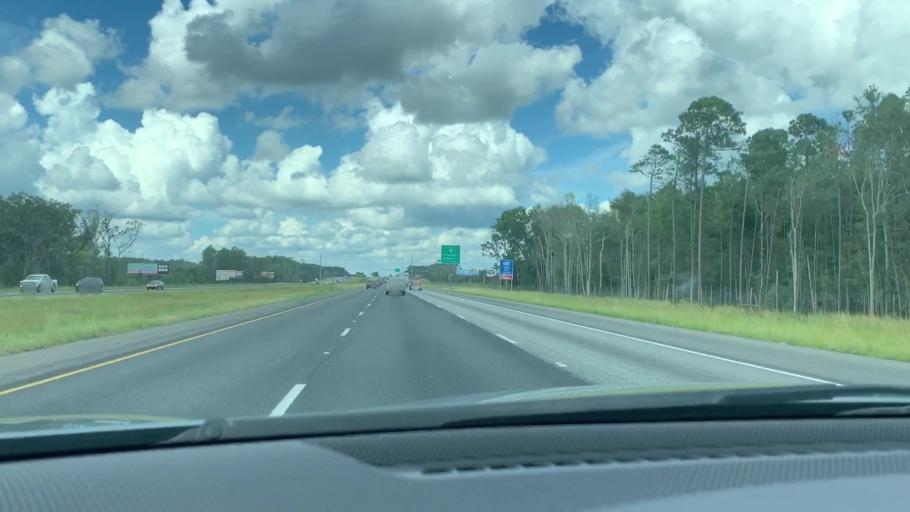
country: US
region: Georgia
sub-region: Camden County
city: Kingsland
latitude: 30.7811
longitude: -81.6567
